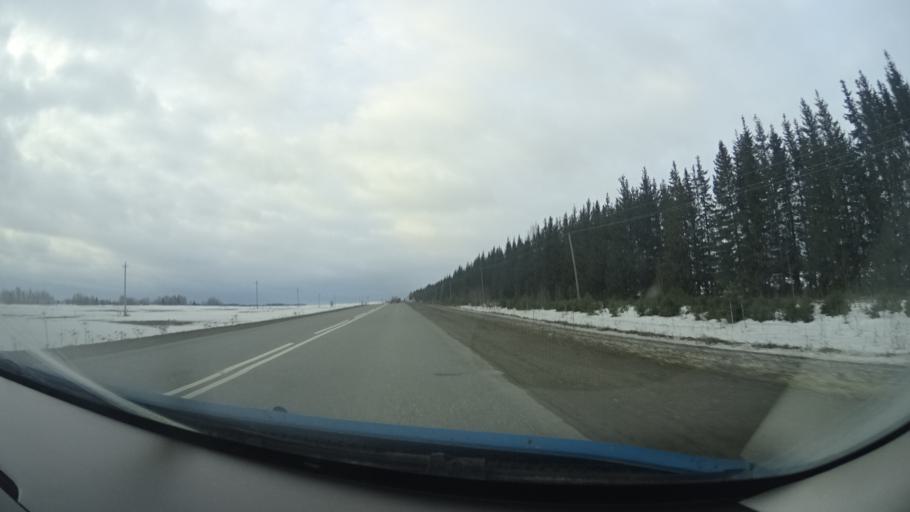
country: RU
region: Perm
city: Osa
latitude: 57.2744
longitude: 55.5689
